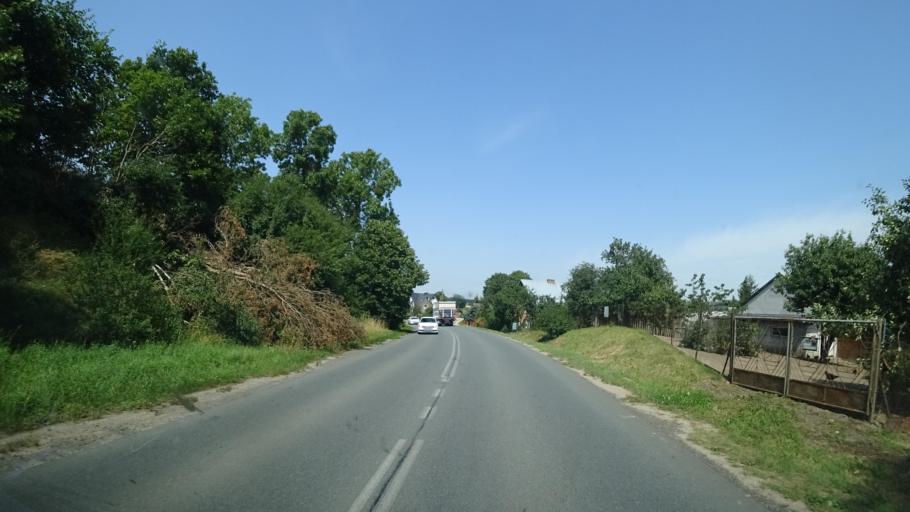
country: PL
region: Pomeranian Voivodeship
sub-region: Powiat koscierski
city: Lipusz
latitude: 54.0742
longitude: 17.8026
